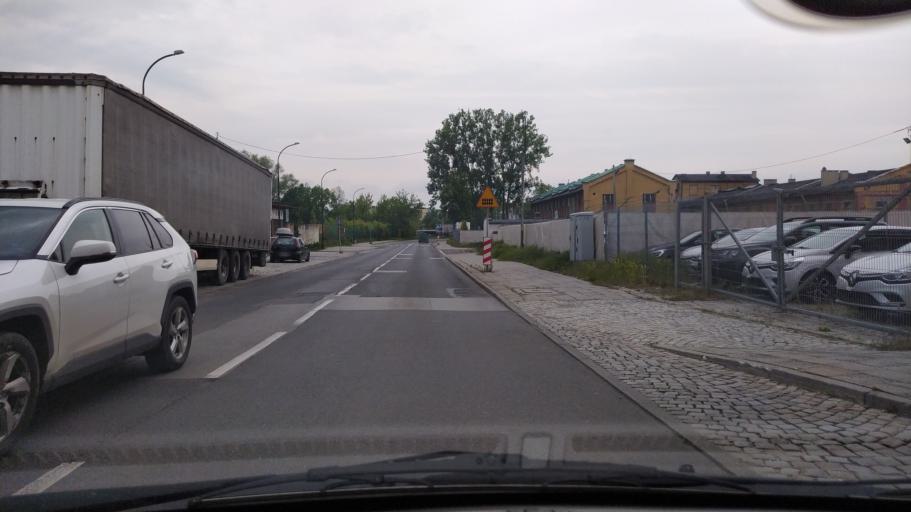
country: PL
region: Silesian Voivodeship
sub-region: Powiat gliwicki
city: Przyszowice
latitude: 50.2905
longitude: 18.7443
